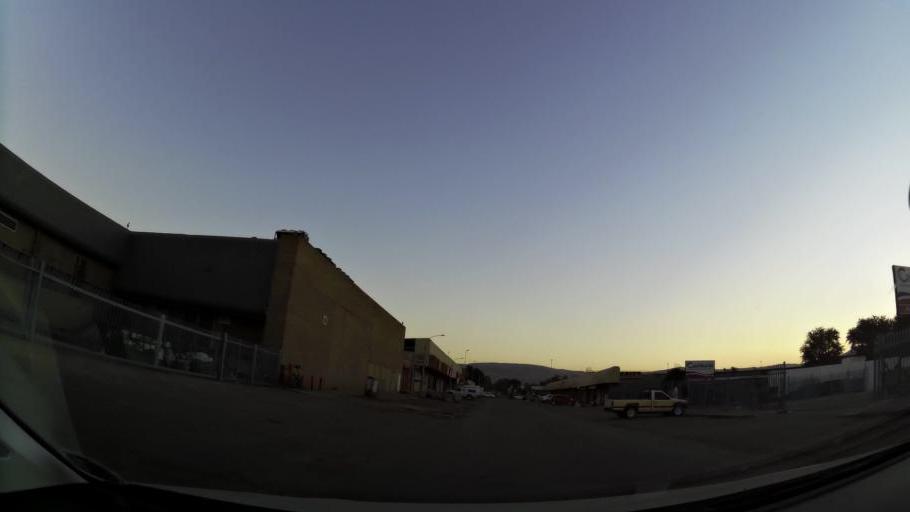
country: ZA
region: North-West
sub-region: Bojanala Platinum District Municipality
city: Rustenburg
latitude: -25.6662
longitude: 27.2386
